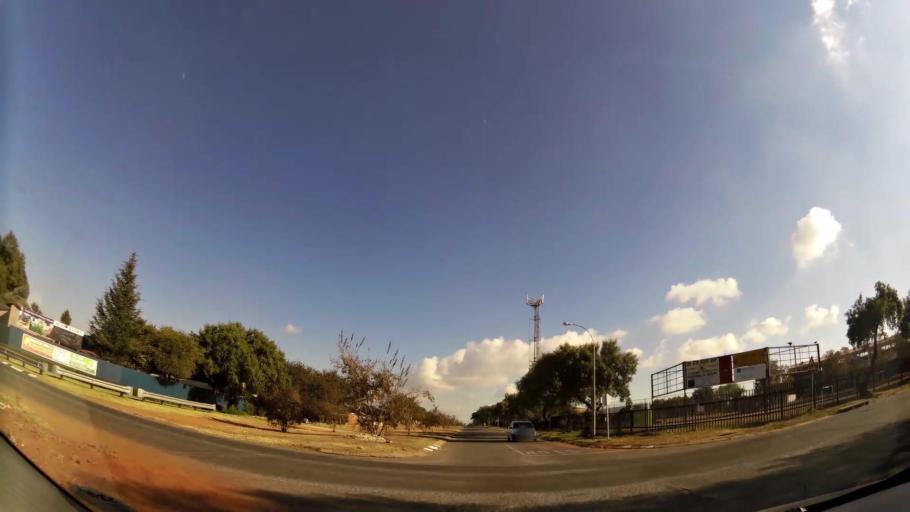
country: ZA
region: Gauteng
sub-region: City of Johannesburg Metropolitan Municipality
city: Roodepoort
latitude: -26.1564
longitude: 27.8284
